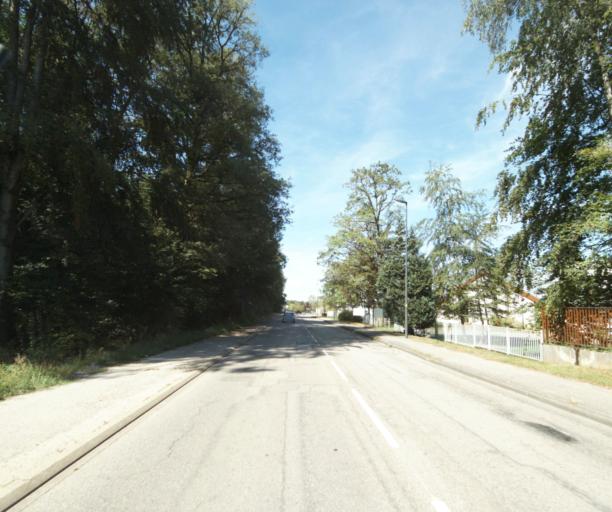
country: FR
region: Lorraine
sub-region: Departement des Vosges
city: Epinal
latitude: 48.1993
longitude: 6.4601
